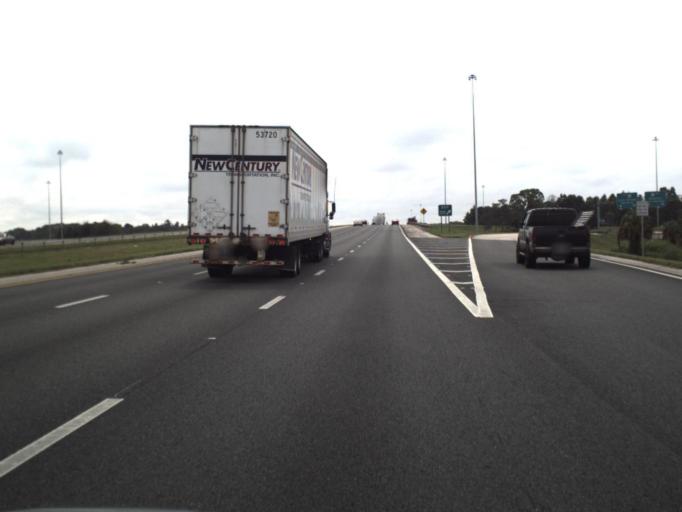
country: US
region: Florida
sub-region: Manatee County
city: Ellenton
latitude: 27.4957
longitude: -82.4745
